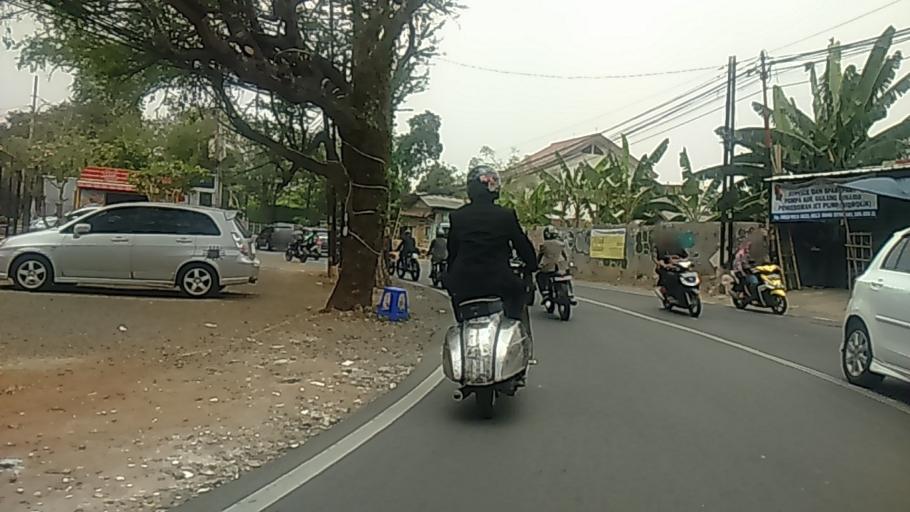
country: ID
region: West Java
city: Pamulang
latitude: -6.3000
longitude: 106.7755
